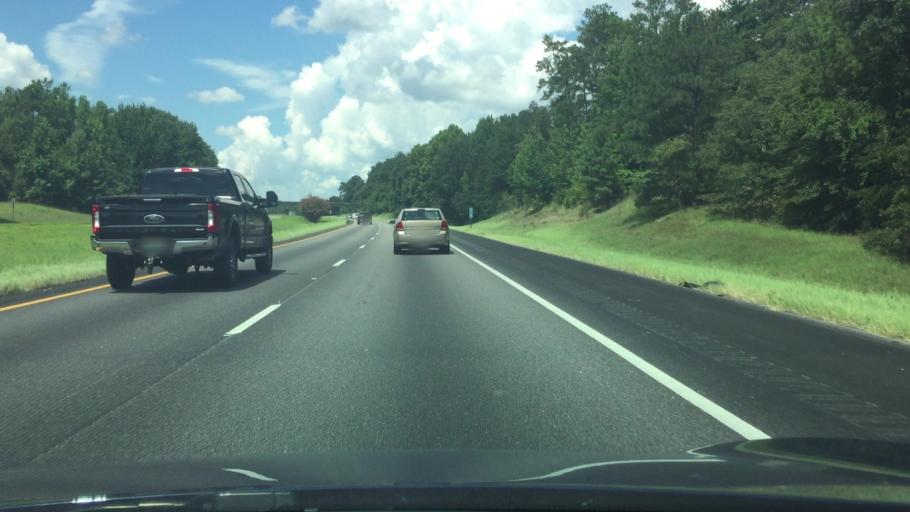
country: US
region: Alabama
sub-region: Elmore County
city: Tallassee
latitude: 32.4379
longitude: -85.8674
